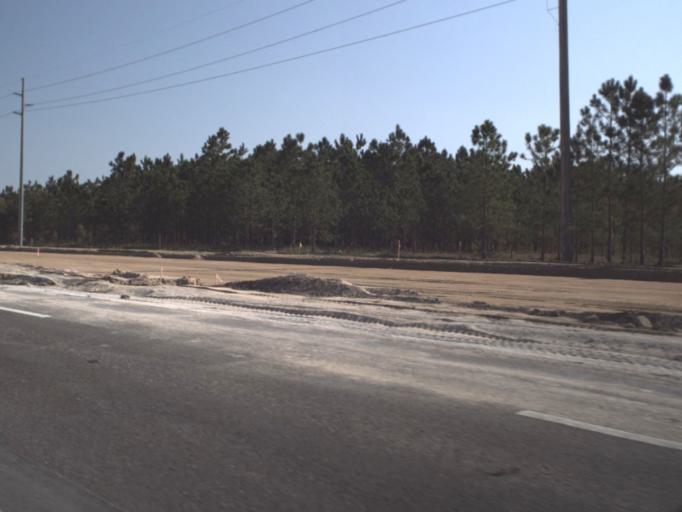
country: US
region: Florida
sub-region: Lake County
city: Clermont
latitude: 28.4760
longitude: -81.7153
